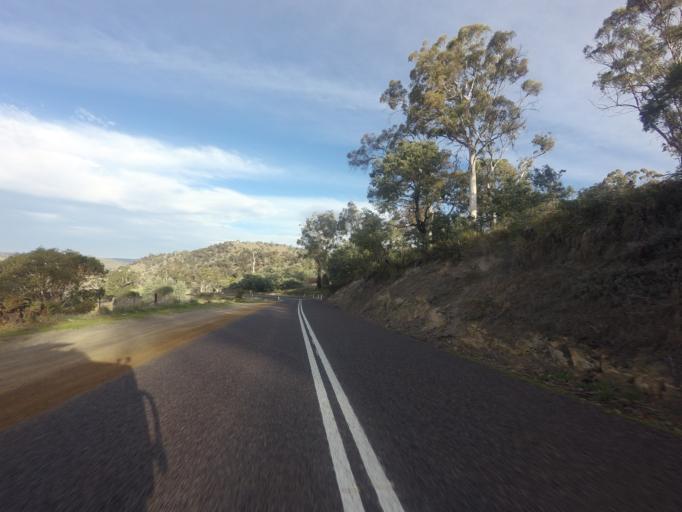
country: AU
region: Tasmania
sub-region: Brighton
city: Bridgewater
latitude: -42.4117
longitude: 147.1237
